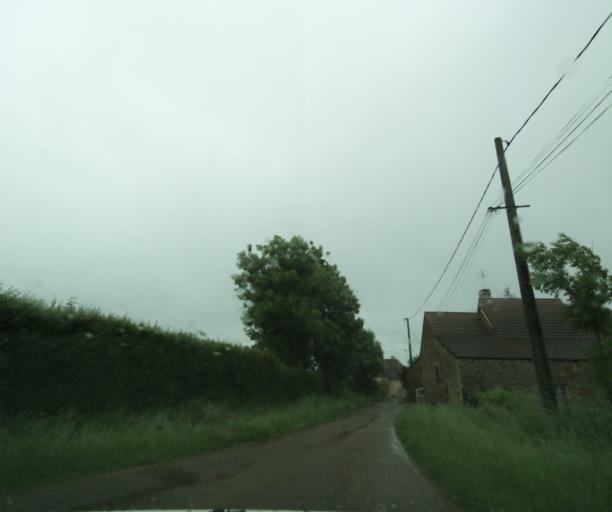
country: FR
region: Bourgogne
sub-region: Departement de Saone-et-Loire
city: Charolles
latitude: 46.3520
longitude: 4.1981
